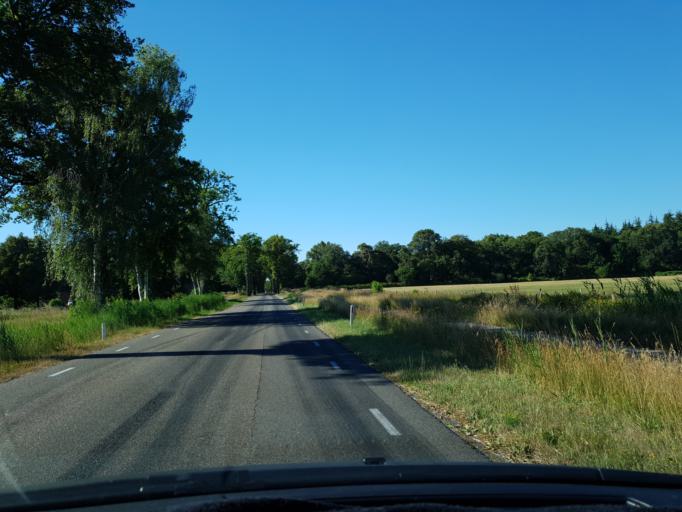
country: NL
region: North Brabant
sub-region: Gemeente Zundert
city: Zundert
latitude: 51.4874
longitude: 4.6086
